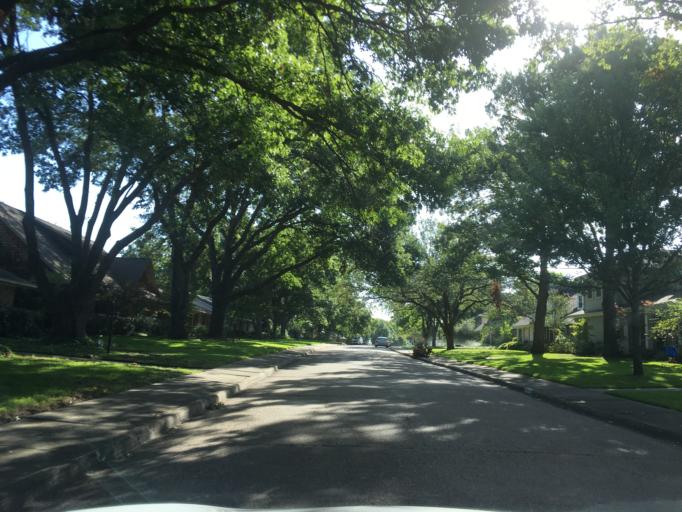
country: US
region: Texas
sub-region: Dallas County
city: Richardson
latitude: 32.8809
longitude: -96.7242
